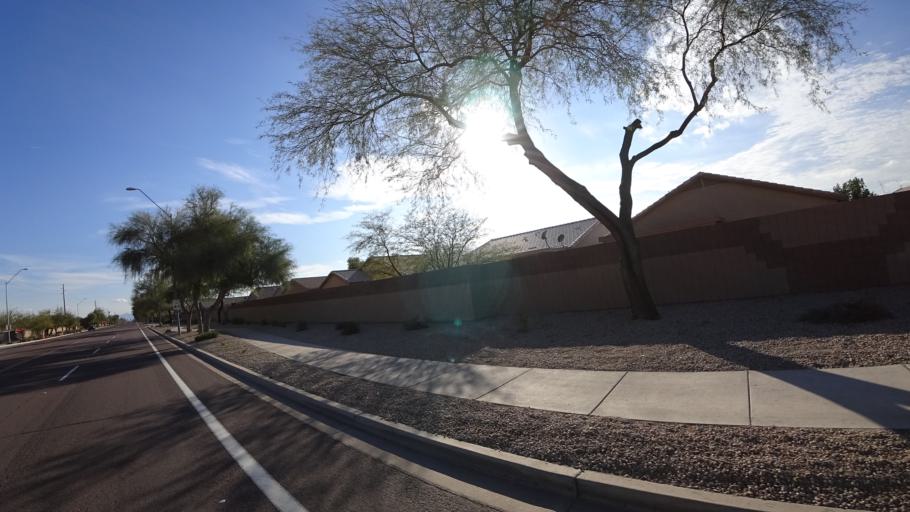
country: US
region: Arizona
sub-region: Maricopa County
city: Sun City
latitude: 33.6738
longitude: -112.2551
